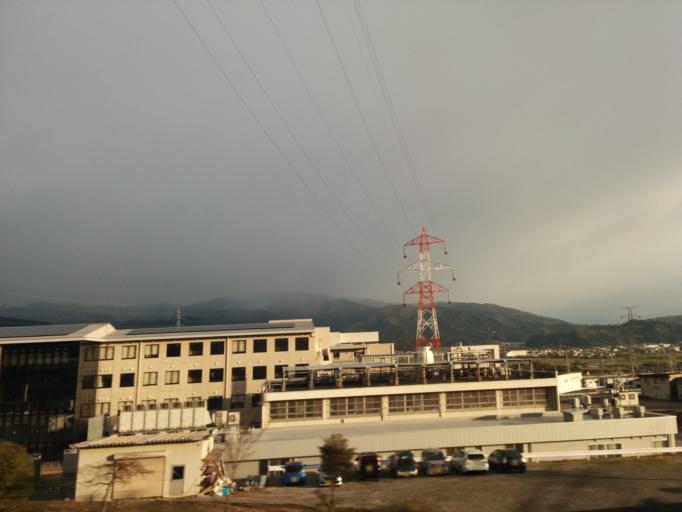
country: JP
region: Gifu
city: Tarui
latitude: 35.3696
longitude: 136.5076
